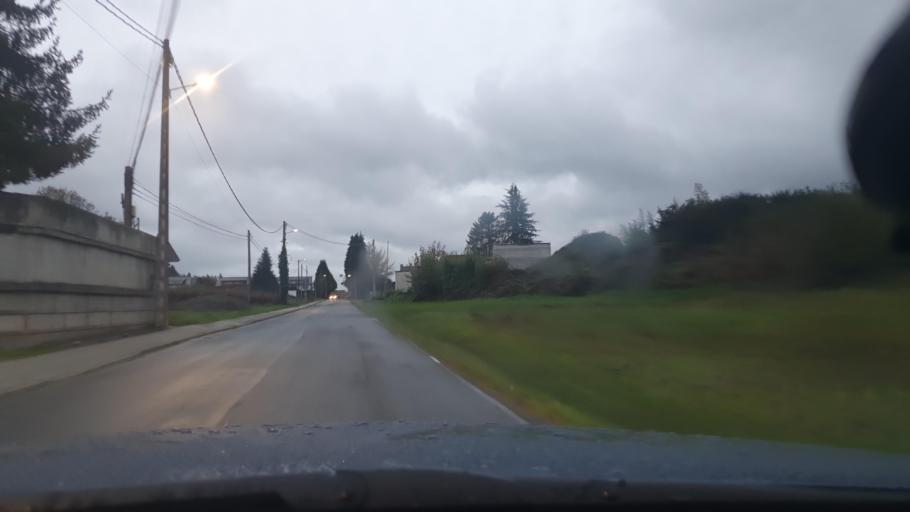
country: ES
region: Galicia
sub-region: Provincia da Coruna
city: Santiago de Compostela
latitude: 42.8504
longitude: -8.5887
